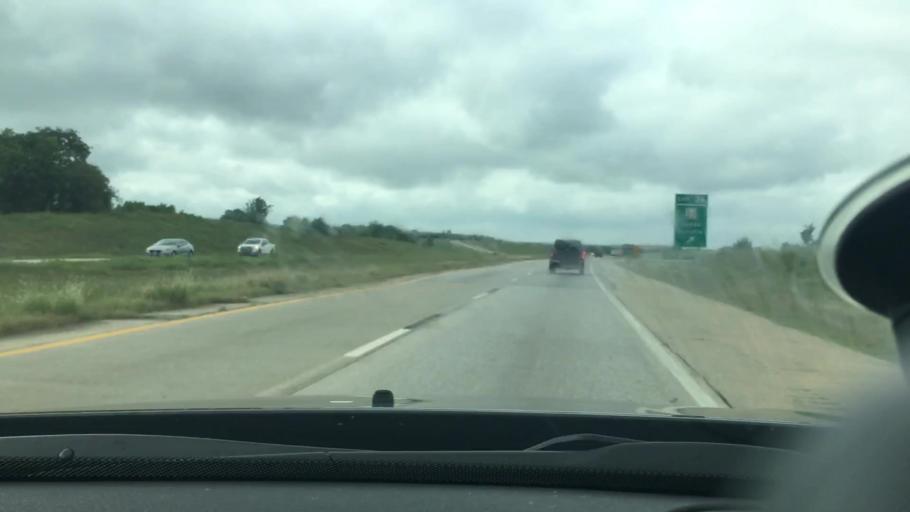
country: US
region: Oklahoma
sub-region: Bryan County
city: Durant
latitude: 34.1381
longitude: -96.2696
